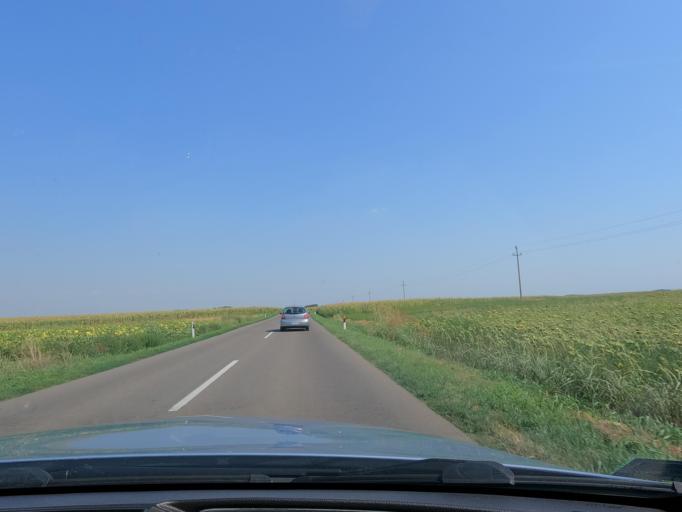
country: RS
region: Autonomna Pokrajina Vojvodina
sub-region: Severnobacki Okrug
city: Backa Topola
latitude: 45.7977
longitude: 19.6666
